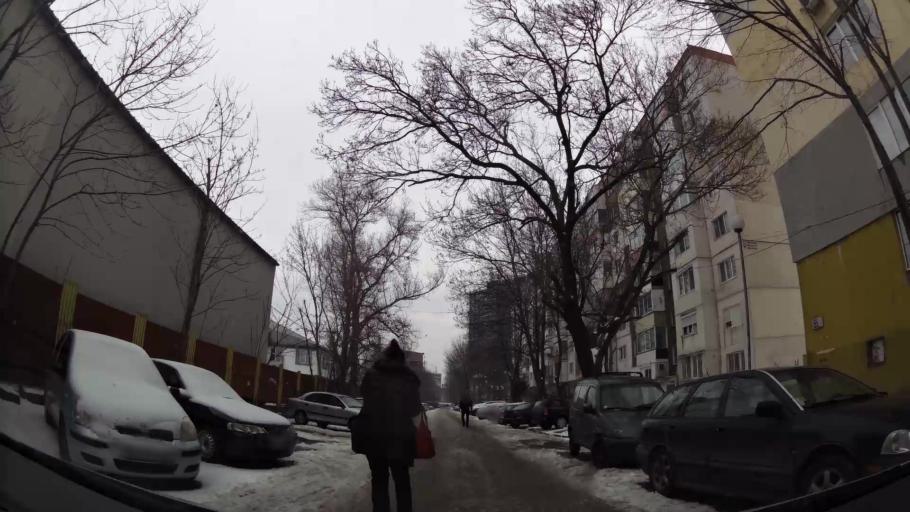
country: BG
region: Sofia-Capital
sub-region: Stolichna Obshtina
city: Sofia
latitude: 42.7134
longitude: 23.3084
